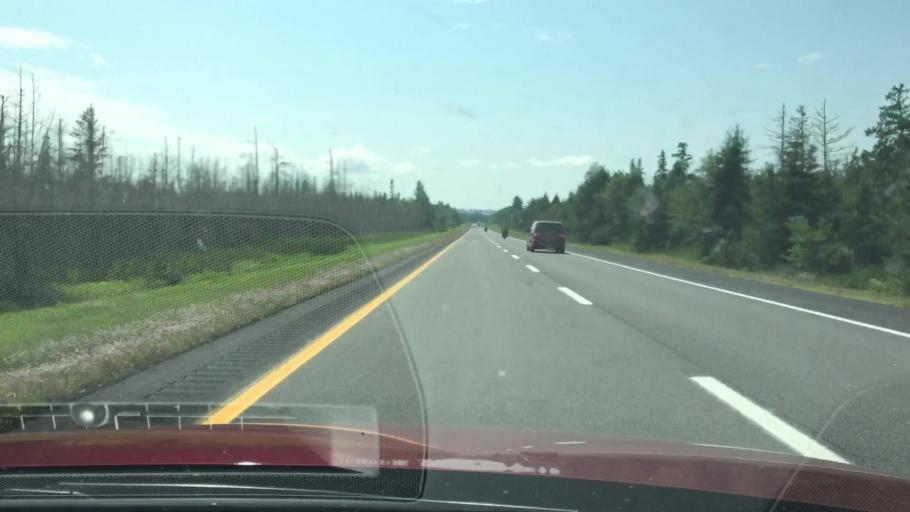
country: US
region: Maine
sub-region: Penobscot County
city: Patten
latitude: 45.9862
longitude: -68.2851
